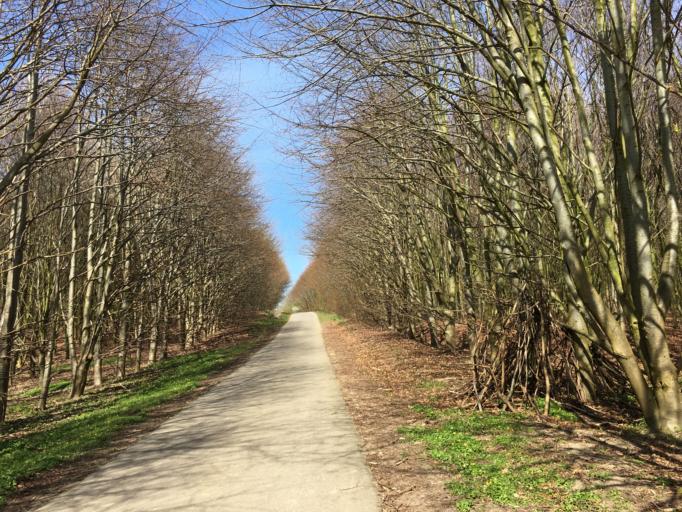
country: DE
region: Schleswig-Holstein
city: Nottfeld
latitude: 54.5894
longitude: 9.8016
